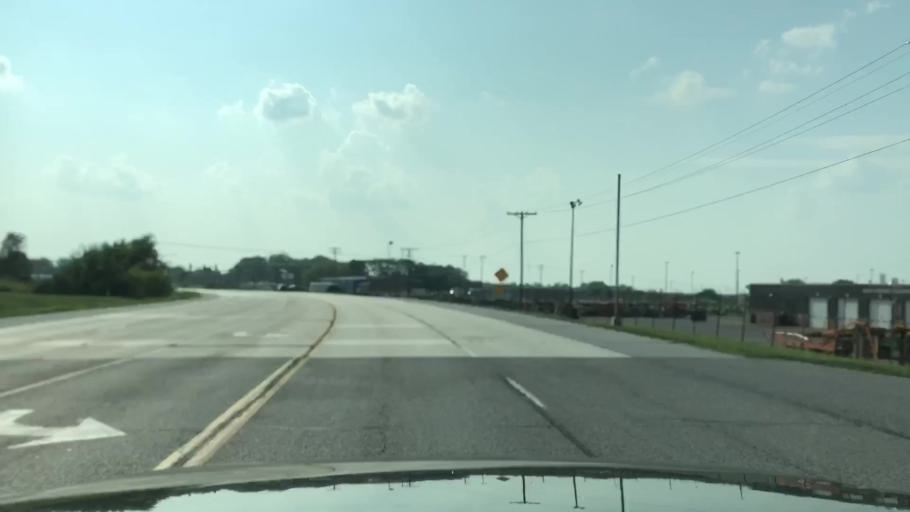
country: US
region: Missouri
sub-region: Saint Charles County
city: Wentzville
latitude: 38.8275
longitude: -90.8315
